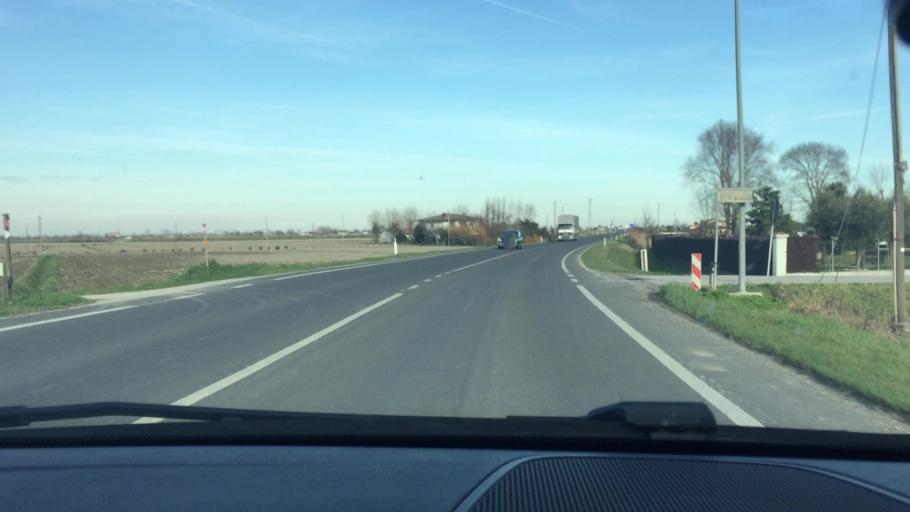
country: IT
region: Veneto
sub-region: Provincia di Padova
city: Correzzola
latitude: 45.2115
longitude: 12.0979
